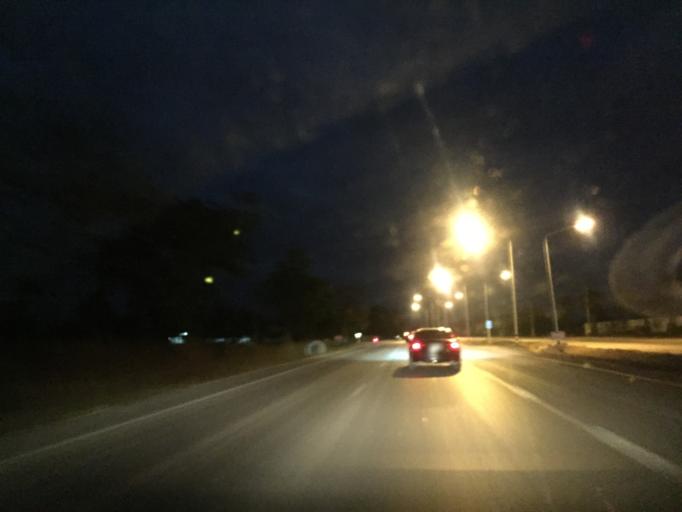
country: TH
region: Changwat Nong Bua Lamphu
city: Na Klang
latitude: 17.2929
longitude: 102.2610
